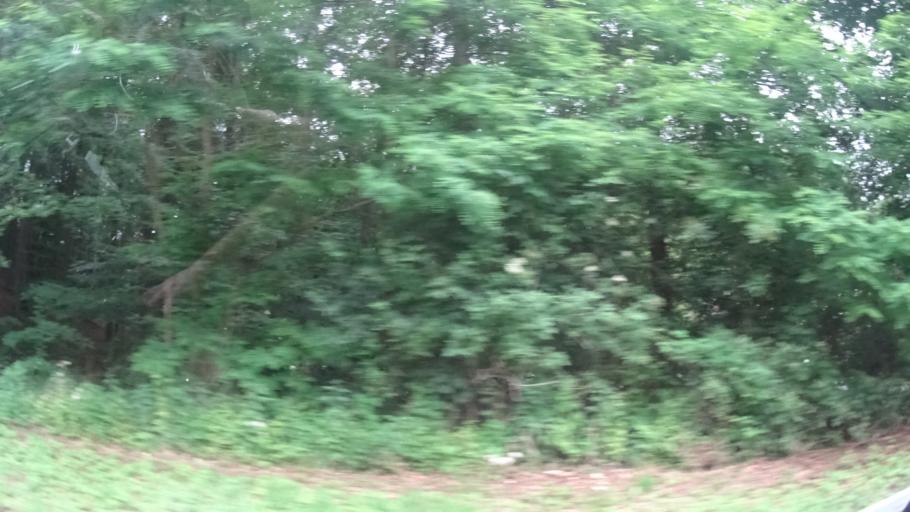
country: DE
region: Bavaria
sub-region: Regierungsbezirk Unterfranken
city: Johannesberg
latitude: 50.0507
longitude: 9.1118
